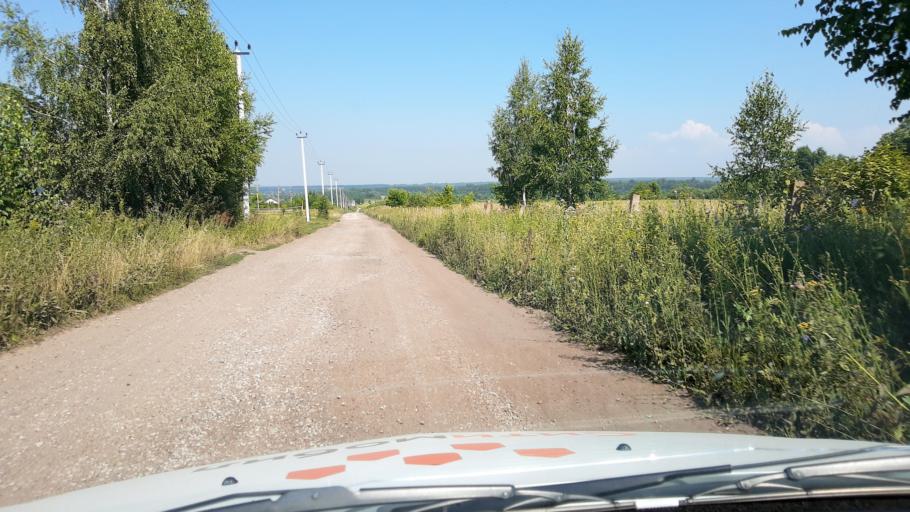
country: RU
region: Bashkortostan
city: Kabakovo
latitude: 54.7069
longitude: 56.1777
